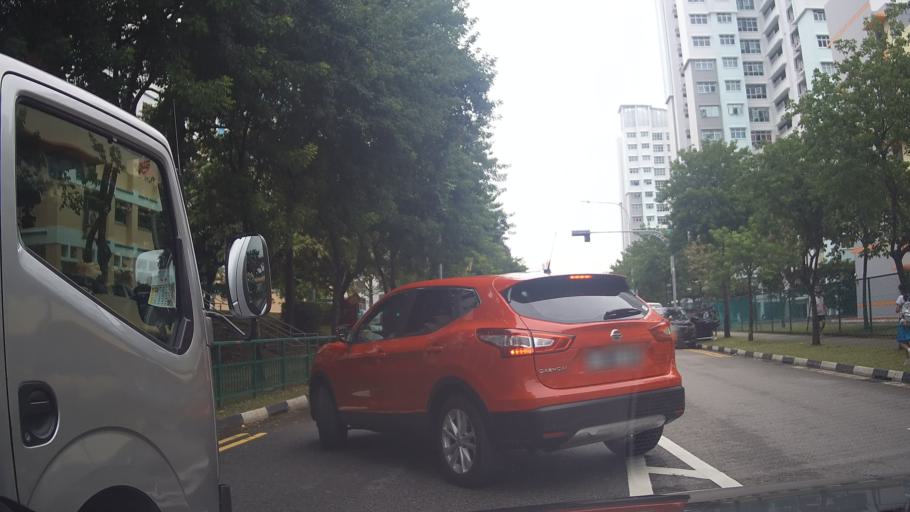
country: MY
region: Johor
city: Johor Bahru
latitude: 1.4470
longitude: 103.8012
